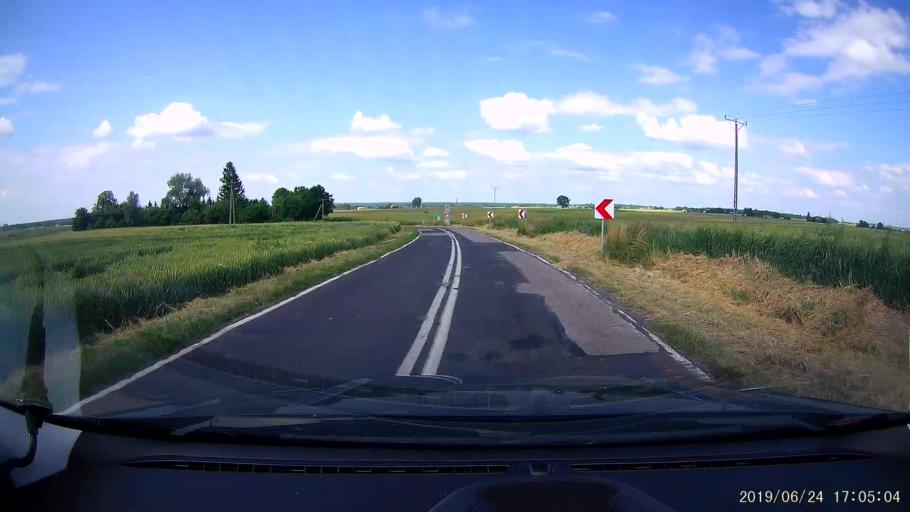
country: PL
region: Lublin Voivodeship
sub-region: Powiat hrubieszowski
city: Dolhobyczow
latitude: 50.5709
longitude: 23.9614
